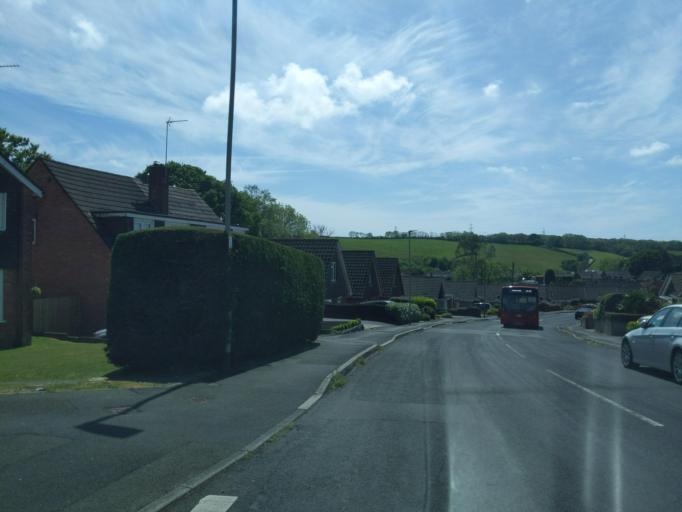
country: GB
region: England
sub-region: Devon
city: Ivybridge
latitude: 50.3903
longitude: -3.9300
